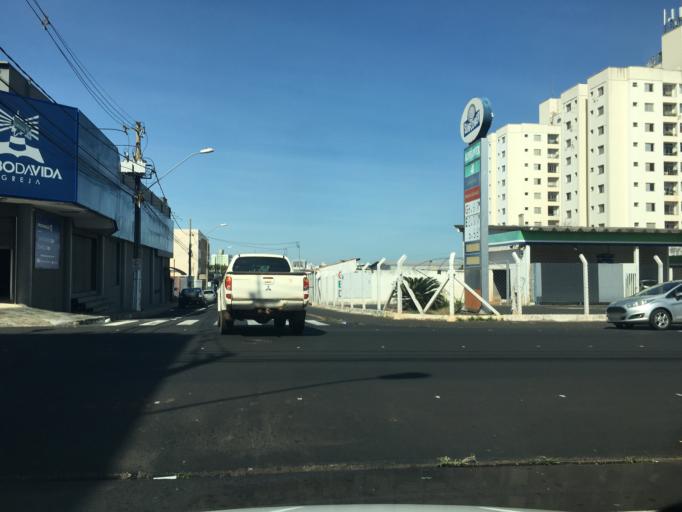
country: BR
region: Minas Gerais
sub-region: Uberlandia
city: Uberlandia
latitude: -18.8986
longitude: -48.2633
